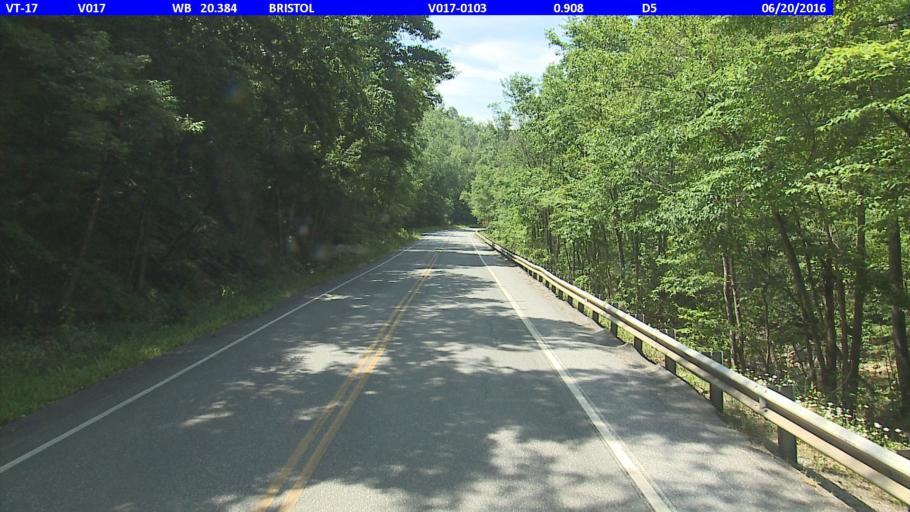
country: US
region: Vermont
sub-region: Addison County
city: Bristol
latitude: 44.1566
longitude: -73.0421
